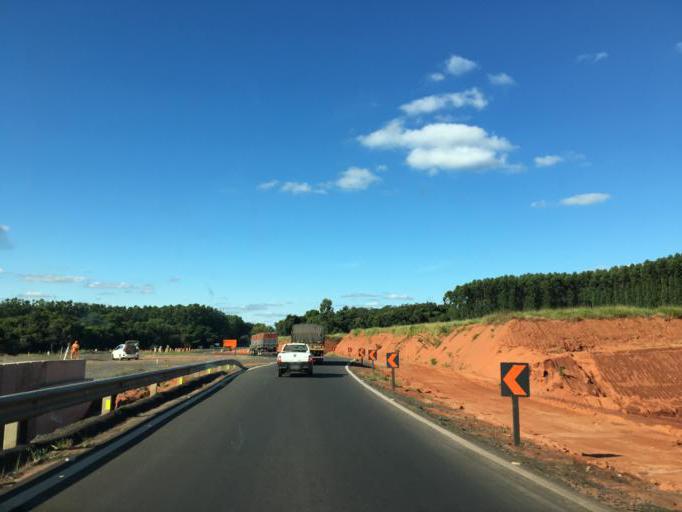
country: BR
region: Sao Paulo
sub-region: Duartina
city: Duartina
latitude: -22.5119
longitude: -49.3028
